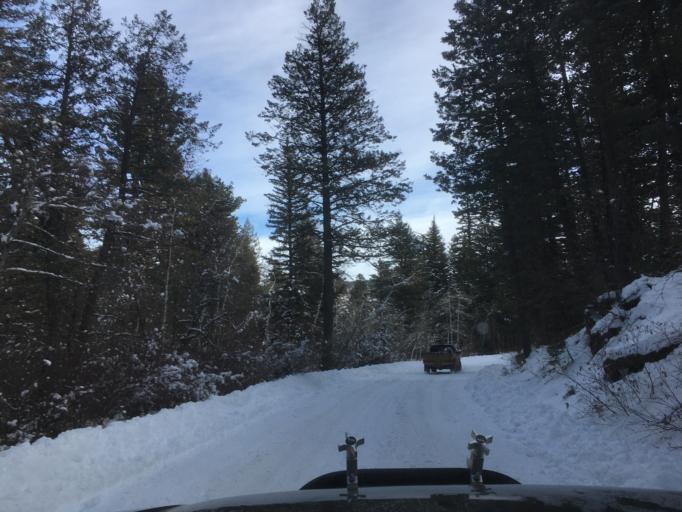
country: US
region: Wyoming
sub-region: Albany County
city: Laramie
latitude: 40.9187
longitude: -105.5105
